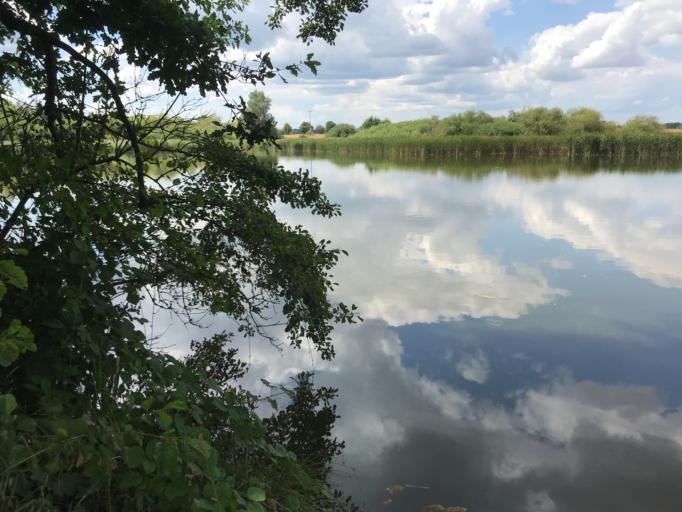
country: CZ
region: Jihocesky
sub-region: Okres Jindrichuv Hradec
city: Lomnice nad Luznici
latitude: 49.0870
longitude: 14.7122
